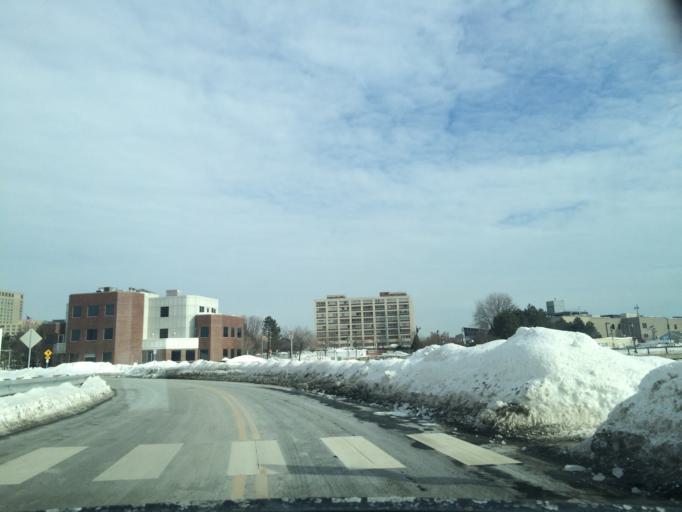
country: US
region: Massachusetts
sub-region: Suffolk County
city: South Boston
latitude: 42.3427
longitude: -71.0390
